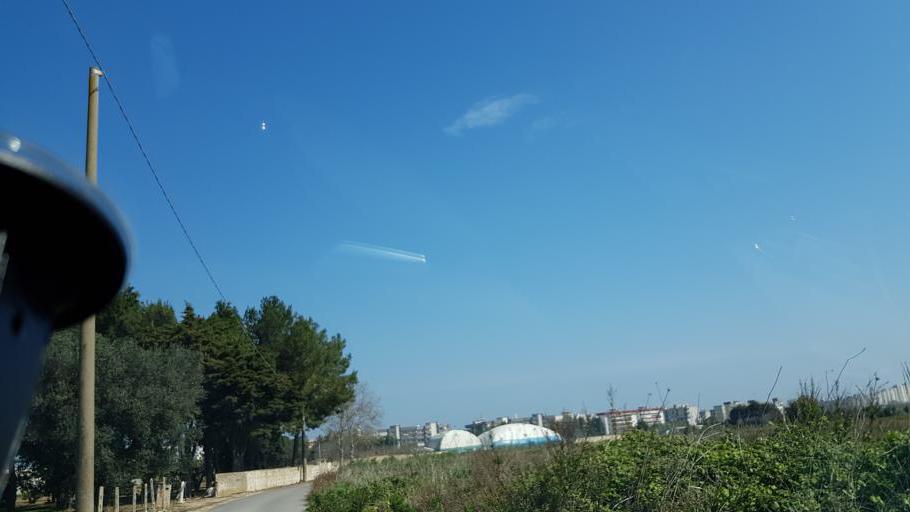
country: IT
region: Apulia
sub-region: Provincia di Brindisi
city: Brindisi
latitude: 40.6132
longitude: 17.9300
